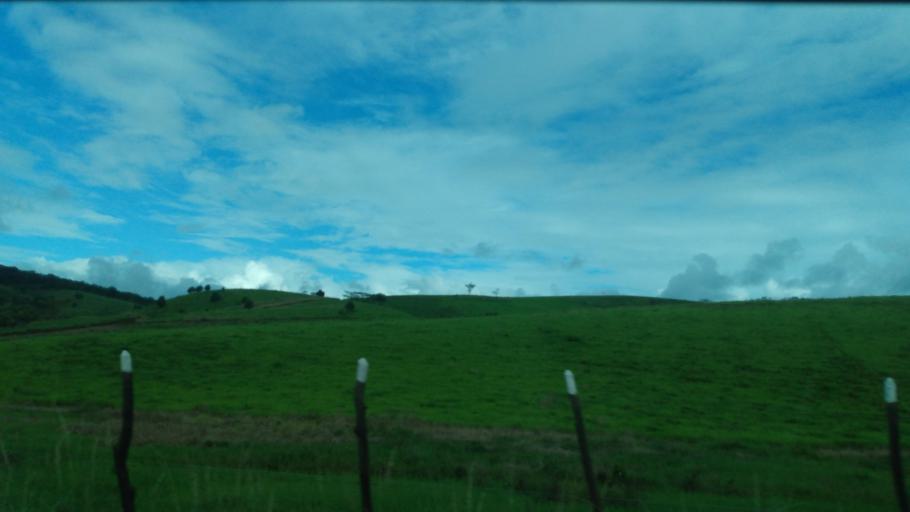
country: BR
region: Pernambuco
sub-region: Catende
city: Catende
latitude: -8.7092
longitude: -35.7645
